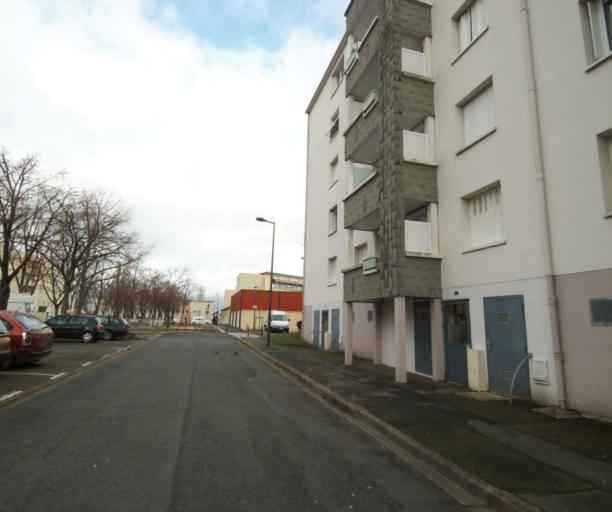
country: FR
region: Pays de la Loire
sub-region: Departement de la Sarthe
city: Le Mans
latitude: 47.9725
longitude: 0.2085
